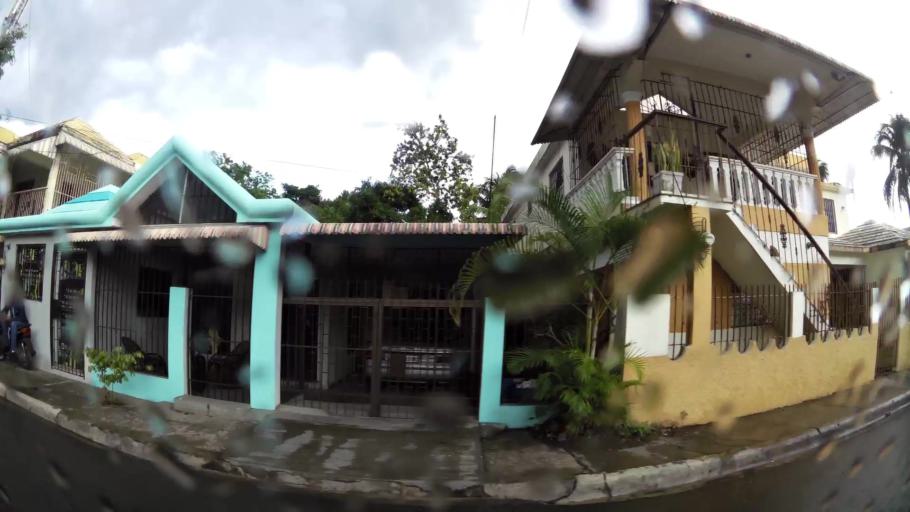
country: DO
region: Monsenor Nouel
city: Bonao
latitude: 18.9356
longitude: -70.4038
